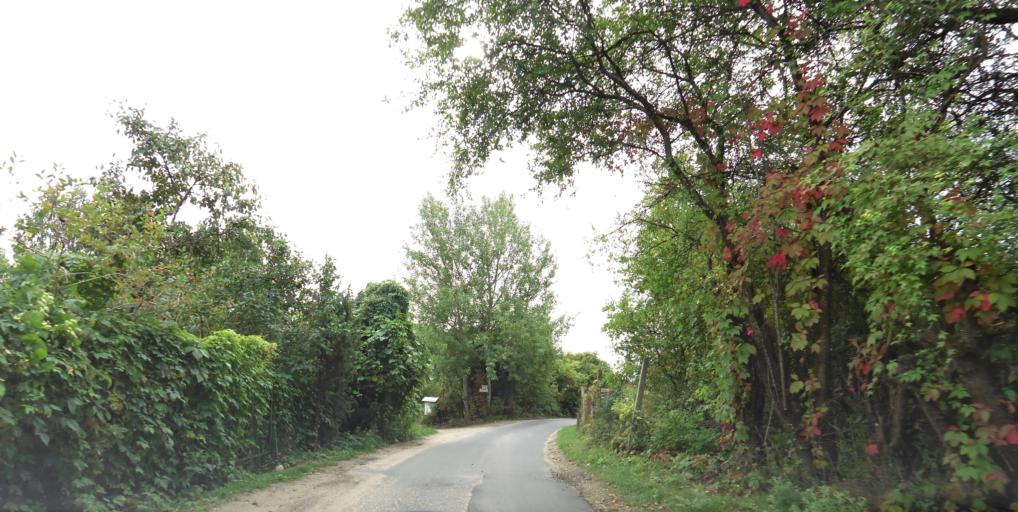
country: LT
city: Grigiskes
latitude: 54.7562
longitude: 25.0287
